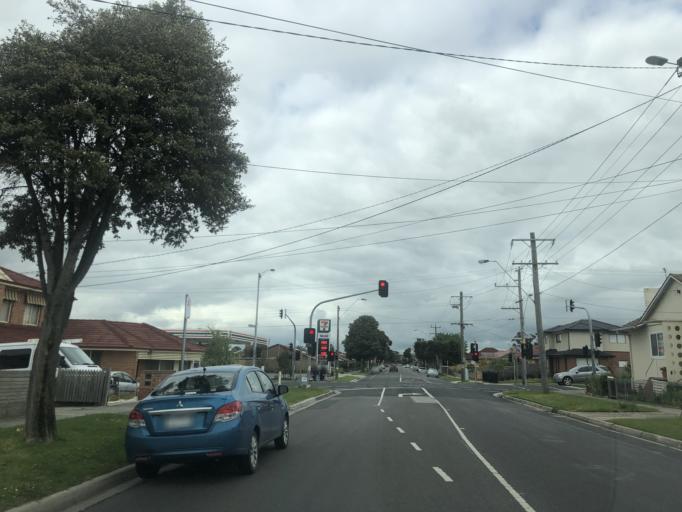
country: AU
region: Victoria
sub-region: Greater Dandenong
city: Dandenong North
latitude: -37.9691
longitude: 145.2113
